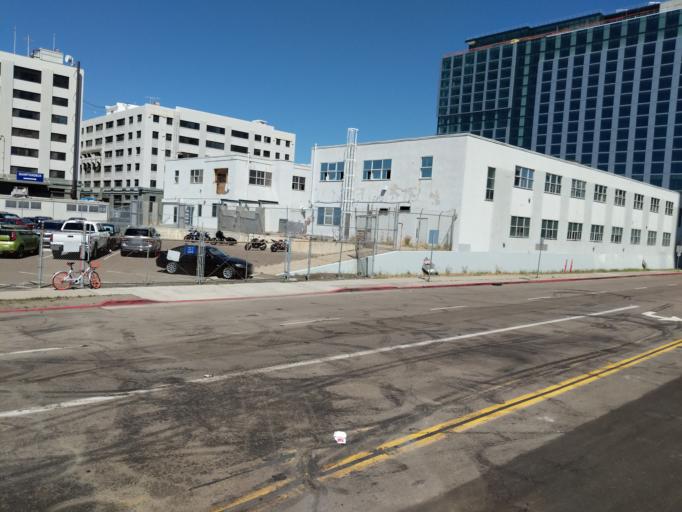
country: US
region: California
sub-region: San Diego County
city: San Diego
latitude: 32.7148
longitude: -117.1710
